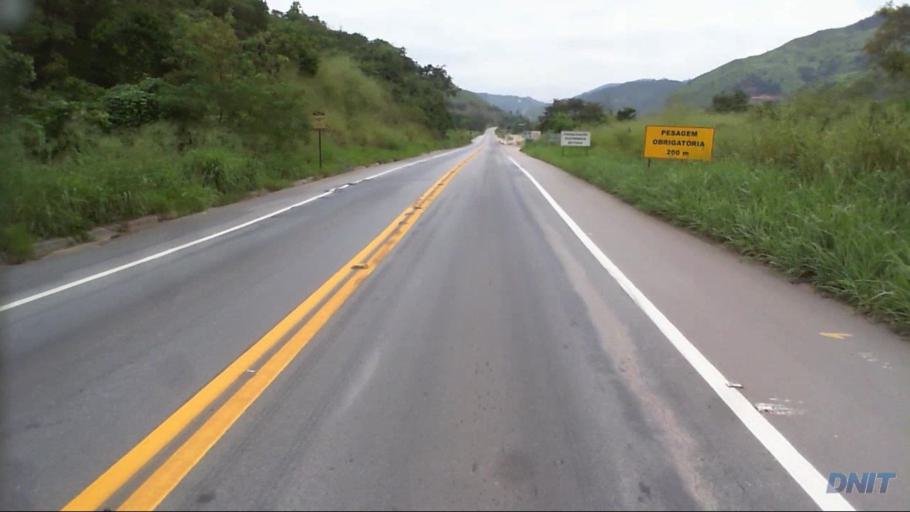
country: BR
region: Minas Gerais
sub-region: Timoteo
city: Timoteo
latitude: -19.5931
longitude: -42.7396
